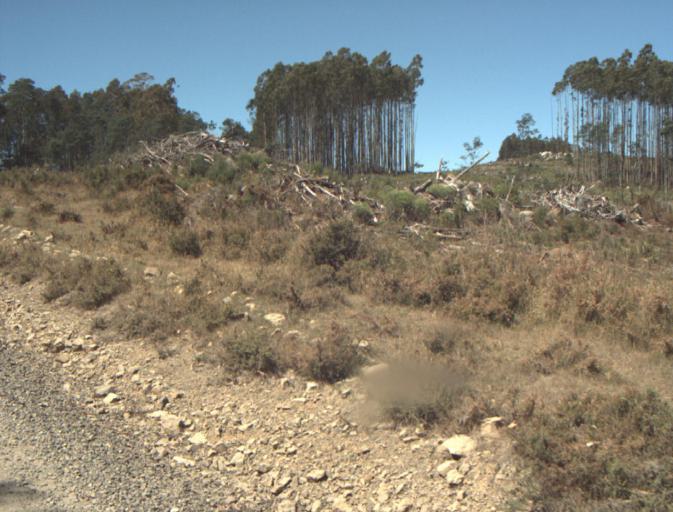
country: AU
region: Tasmania
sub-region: Dorset
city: Scottsdale
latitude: -41.3282
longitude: 147.4845
